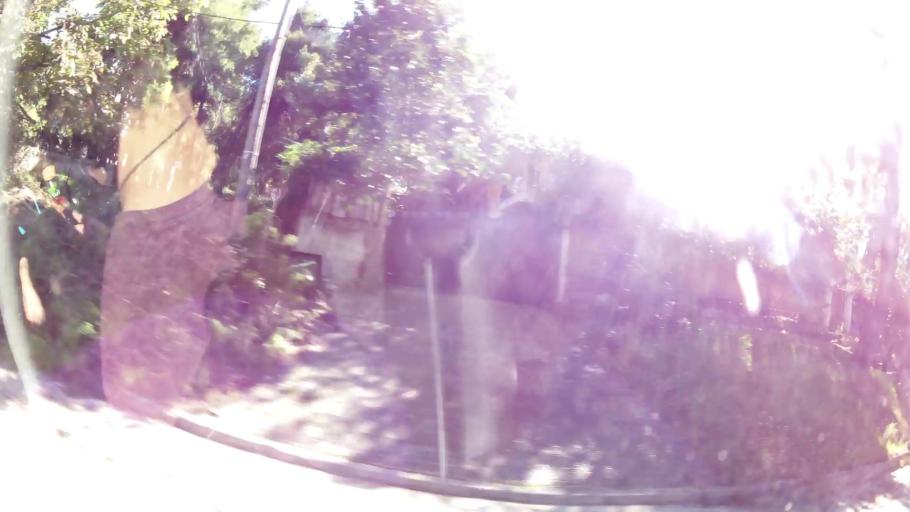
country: GR
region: Attica
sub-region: Nomarchia Anatolikis Attikis
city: Dionysos
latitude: 38.1075
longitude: 23.8765
